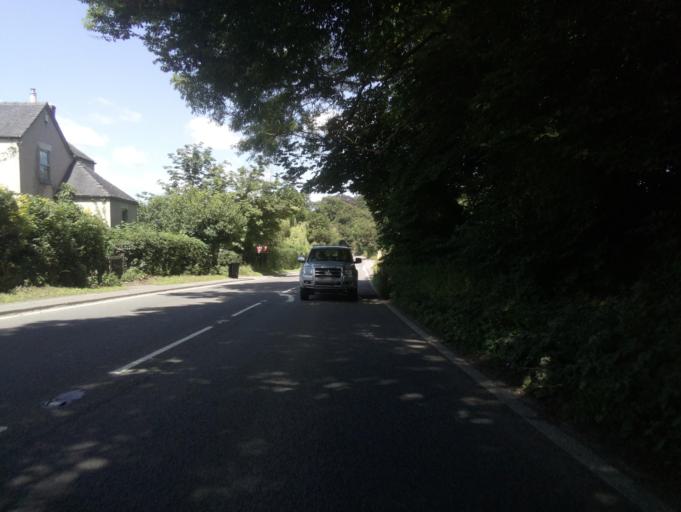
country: GB
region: England
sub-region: Derbyshire
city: Ashbourne
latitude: 53.0270
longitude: -1.7345
